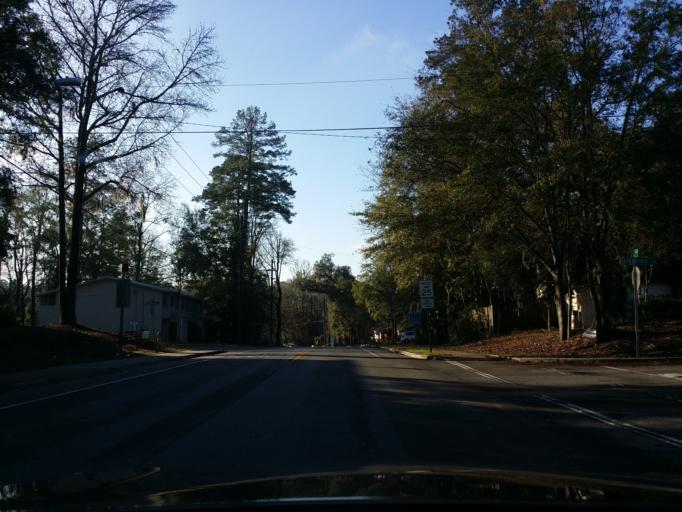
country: US
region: Florida
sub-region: Leon County
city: Tallahassee
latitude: 30.4342
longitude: -84.2125
